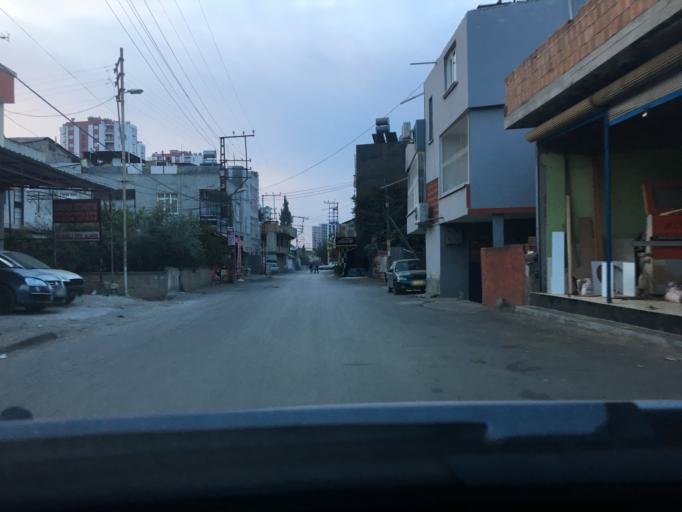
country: TR
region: Adana
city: Seyhan
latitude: 37.0152
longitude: 35.2859
